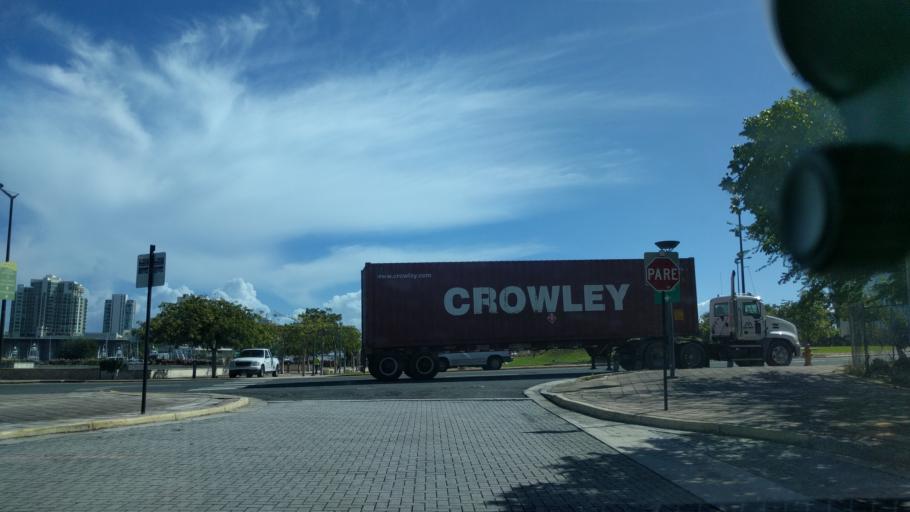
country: PR
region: San Juan
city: San Juan
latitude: 18.4564
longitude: -66.0893
